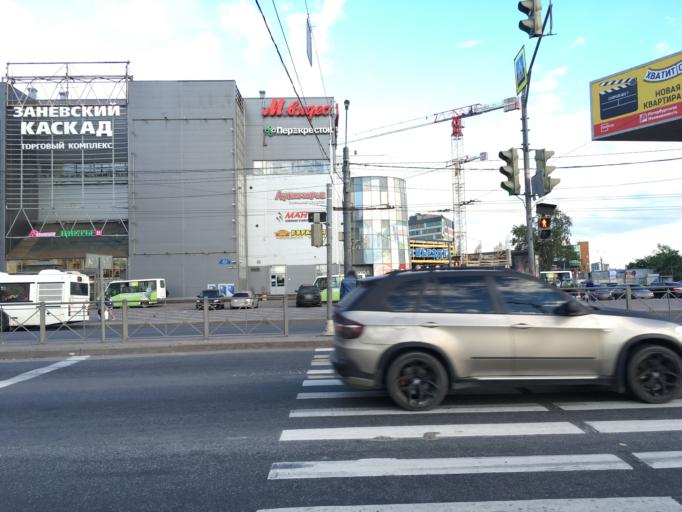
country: RU
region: St.-Petersburg
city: Krasnogvargeisky
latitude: 59.9338
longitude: 30.4363
